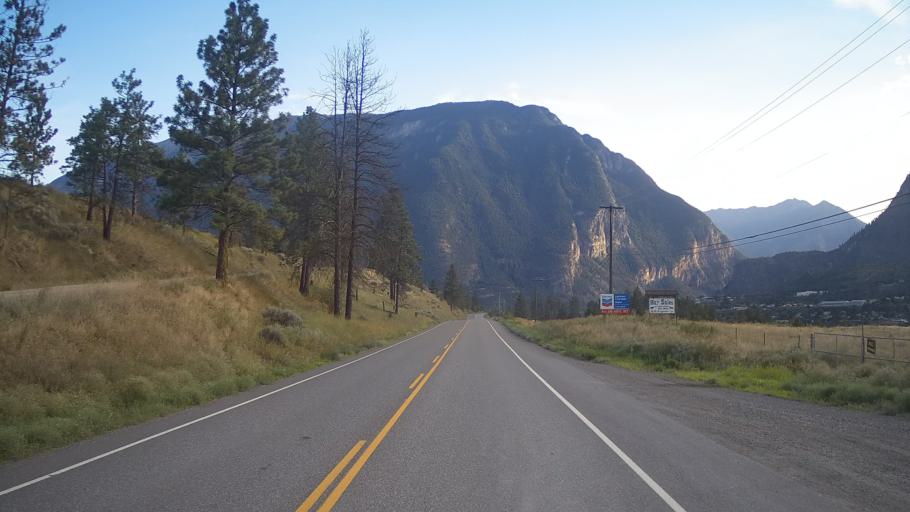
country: CA
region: British Columbia
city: Lillooet
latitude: 50.6990
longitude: -121.9167
